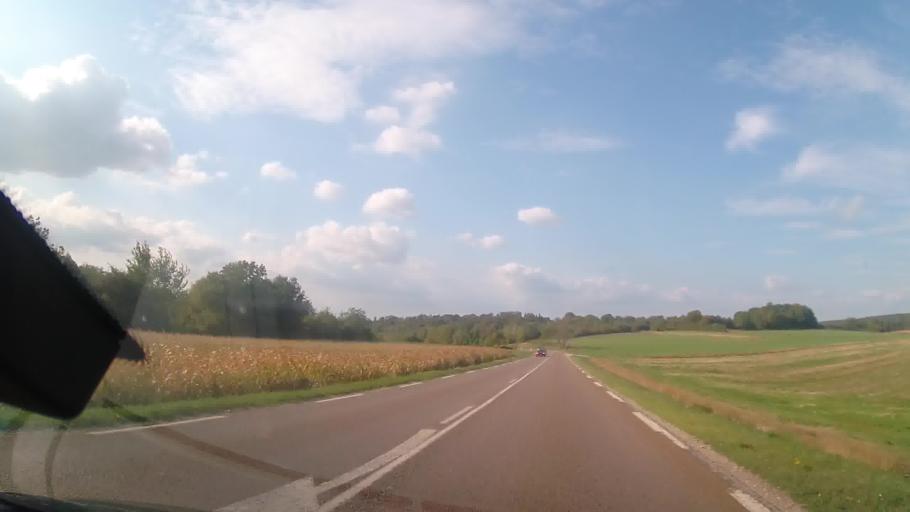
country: FR
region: Franche-Comte
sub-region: Departement du Jura
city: Perrigny
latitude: 46.6424
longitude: 5.5844
